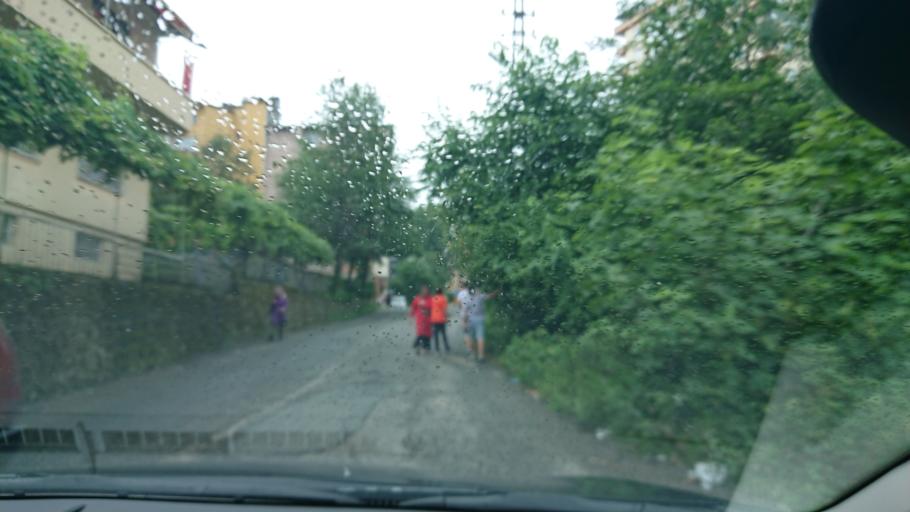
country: TR
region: Rize
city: Rize
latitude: 41.0193
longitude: 40.5166
